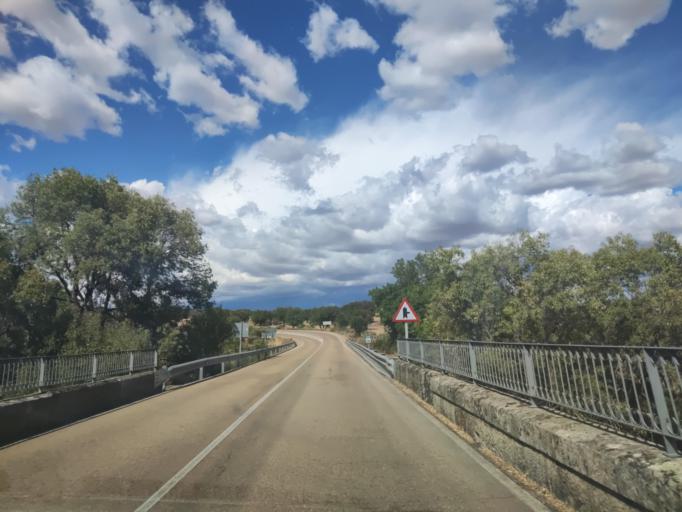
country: ES
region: Castille and Leon
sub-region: Provincia de Salamanca
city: Buenamadre
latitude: 40.8984
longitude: -6.3215
